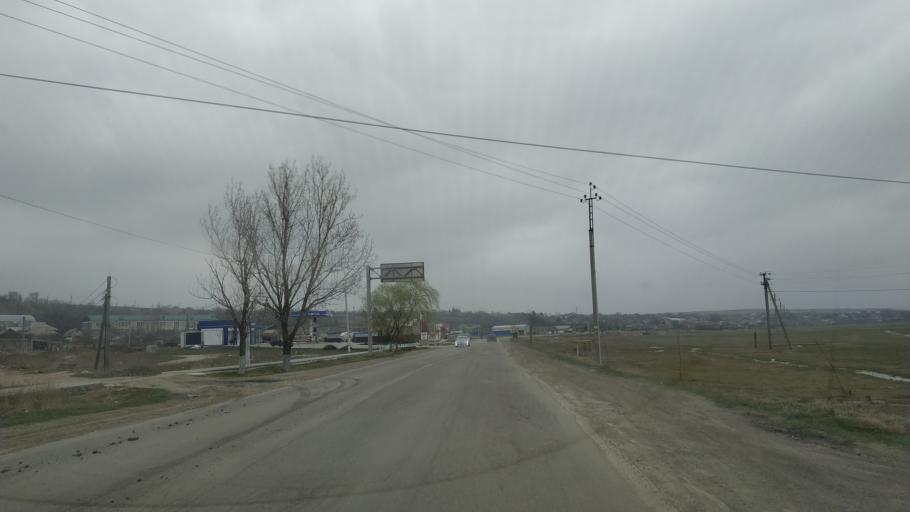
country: MD
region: Gagauzia
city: Comrat
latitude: 46.2938
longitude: 28.6661
